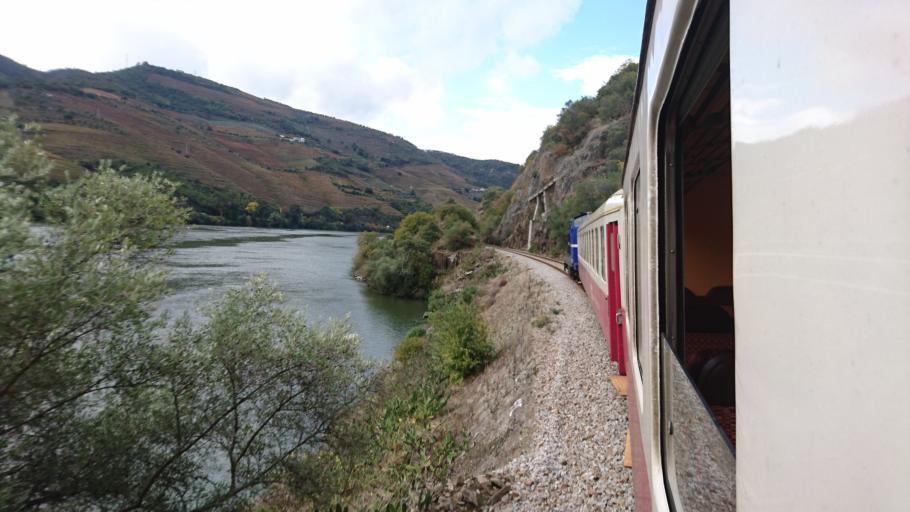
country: PT
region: Viseu
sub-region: Tabuaco
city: Tabuaco
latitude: 41.1602
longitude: -7.5835
